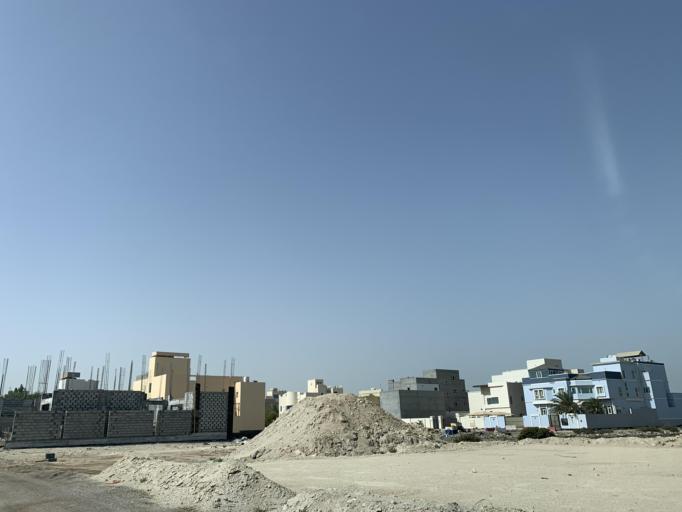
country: BH
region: Northern
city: Sitrah
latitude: 26.1485
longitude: 50.6058
